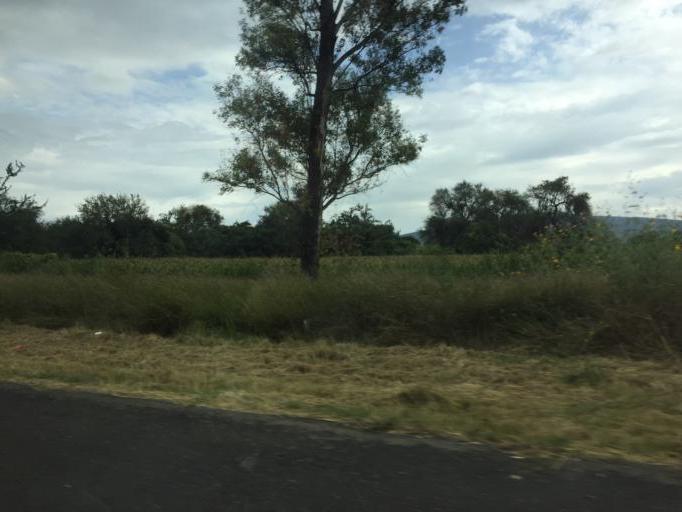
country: MX
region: Jalisco
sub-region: Ocotlan
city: Joconoxtle (La Tuna)
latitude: 20.3801
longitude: -102.6934
